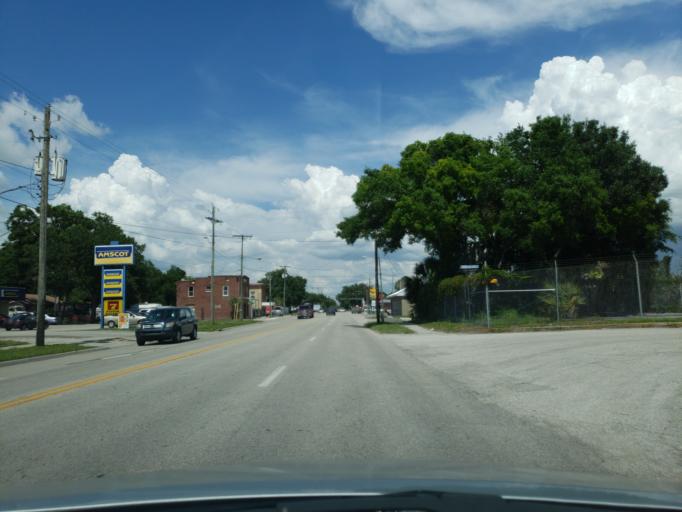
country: US
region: Florida
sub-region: Hillsborough County
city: East Lake-Orient Park
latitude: 27.9612
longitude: -82.4044
